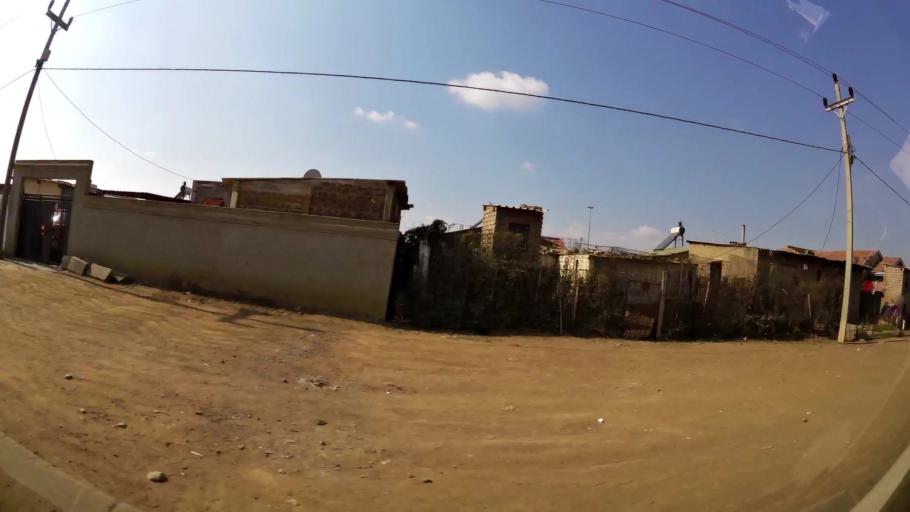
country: ZA
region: Gauteng
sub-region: Ekurhuleni Metropolitan Municipality
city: Springs
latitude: -26.1146
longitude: 28.4752
